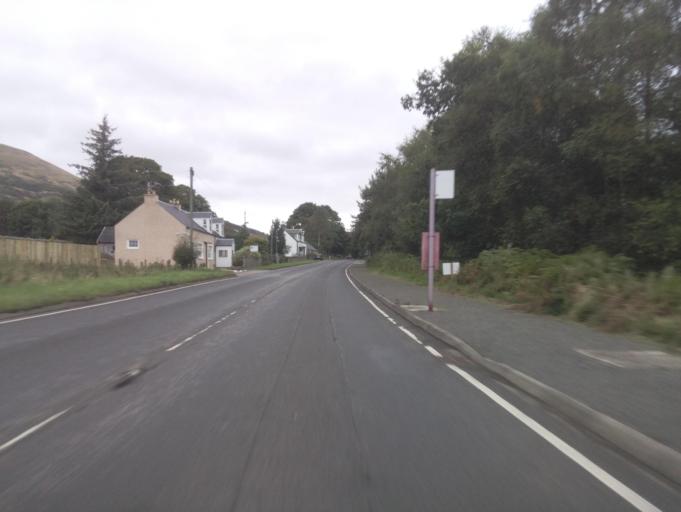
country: GB
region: Scotland
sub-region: Clackmannanshire
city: Dollar
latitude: 56.1835
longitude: -3.6239
